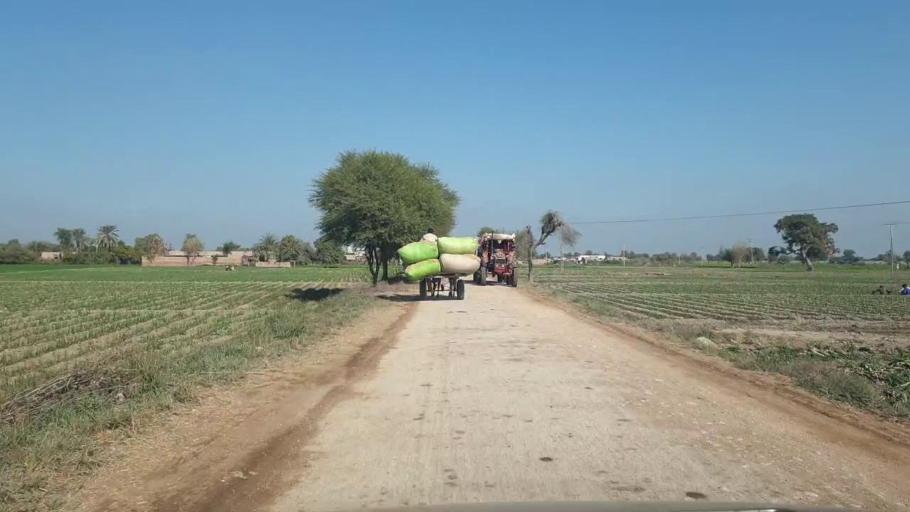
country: PK
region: Sindh
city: Bhit Shah
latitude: 25.8910
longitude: 68.5264
